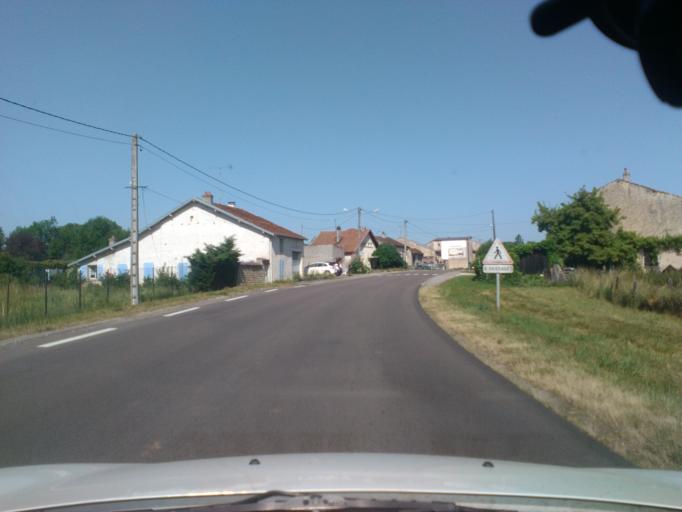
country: FR
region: Lorraine
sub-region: Departement des Vosges
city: Mirecourt
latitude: 48.3085
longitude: 6.1035
